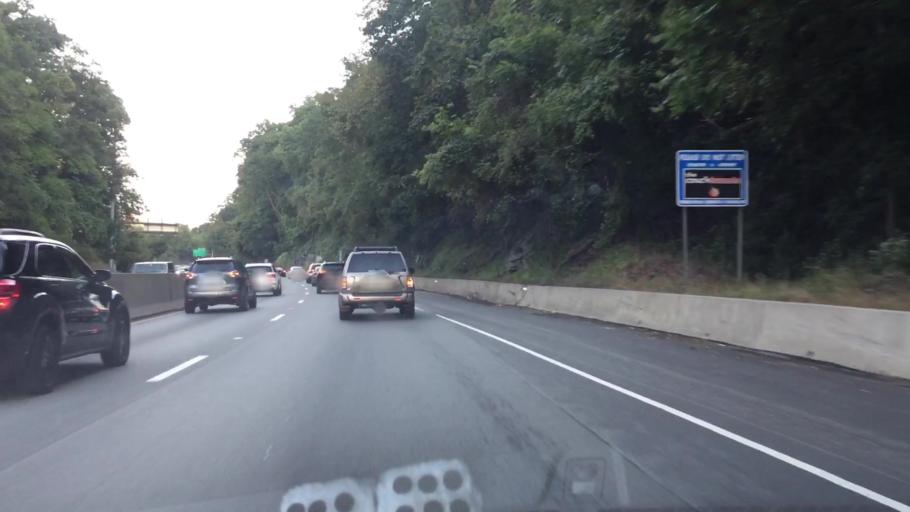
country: US
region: Pennsylvania
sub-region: Montgomery County
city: Narberth
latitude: 40.0377
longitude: -75.2480
